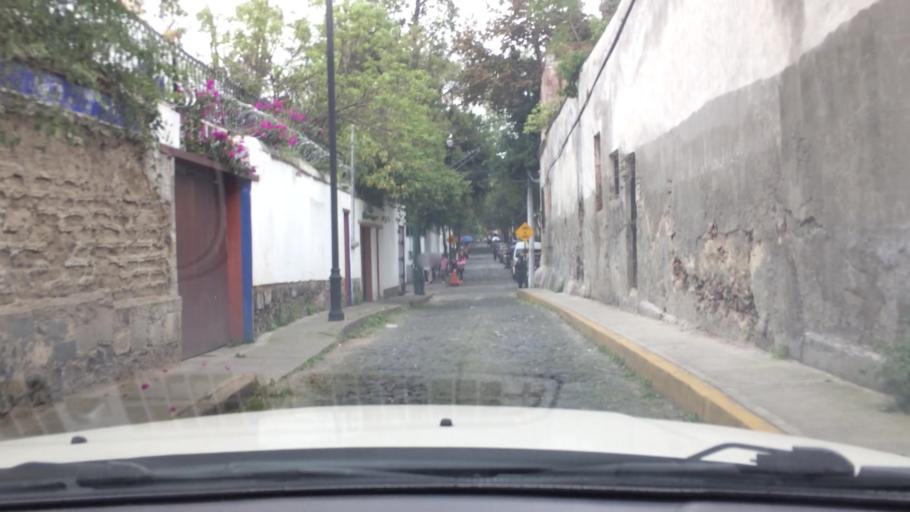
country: MX
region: Mexico City
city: Tlalpan
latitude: 19.2889
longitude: -99.1648
